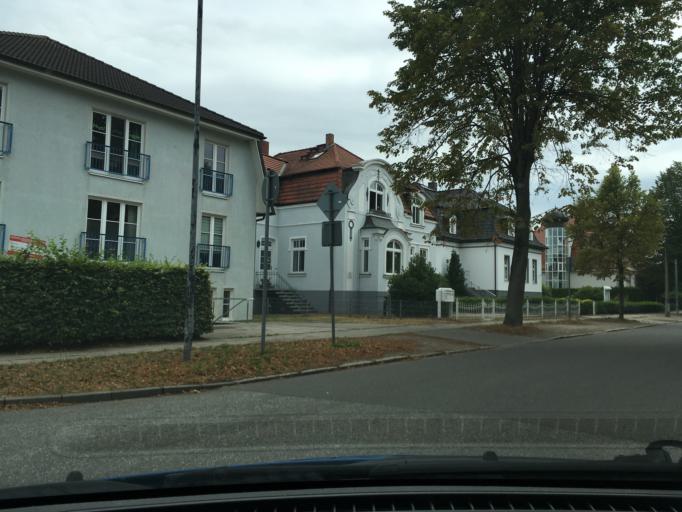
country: DE
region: Mecklenburg-Vorpommern
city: Wittenburg
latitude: 53.5112
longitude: 11.0802
